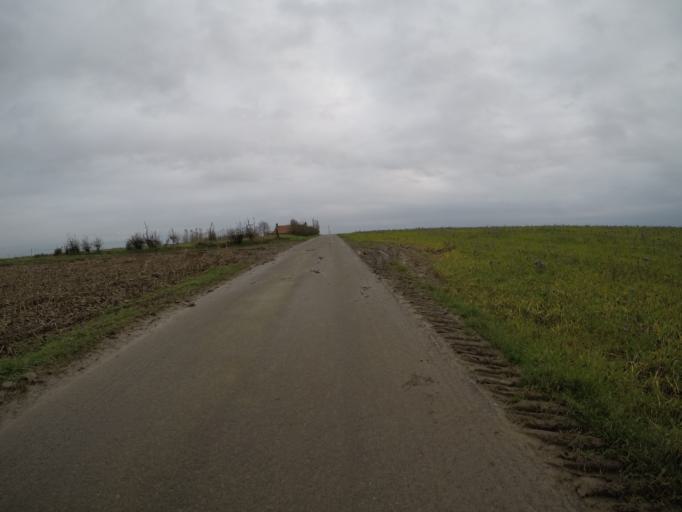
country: BE
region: Flanders
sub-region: Provincie West-Vlaanderen
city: Saint-Yvon
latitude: 50.7815
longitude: 2.8786
